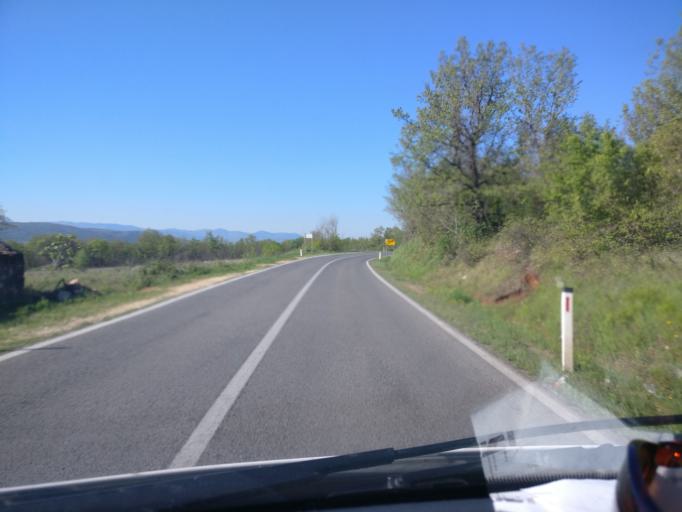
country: BA
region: Federation of Bosnia and Herzegovina
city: Tasovcici
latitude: 43.1328
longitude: 17.7721
